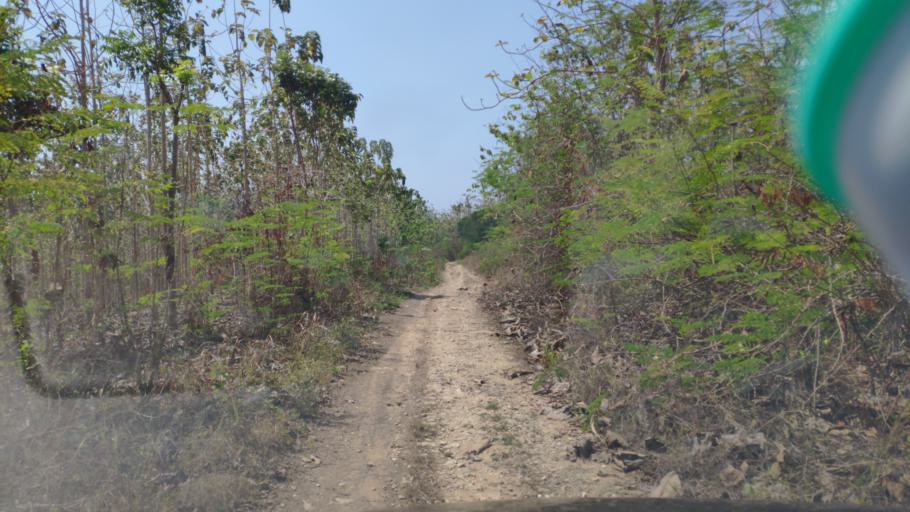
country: ID
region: Central Java
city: Gaplokan
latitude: -6.9126
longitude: 111.2671
